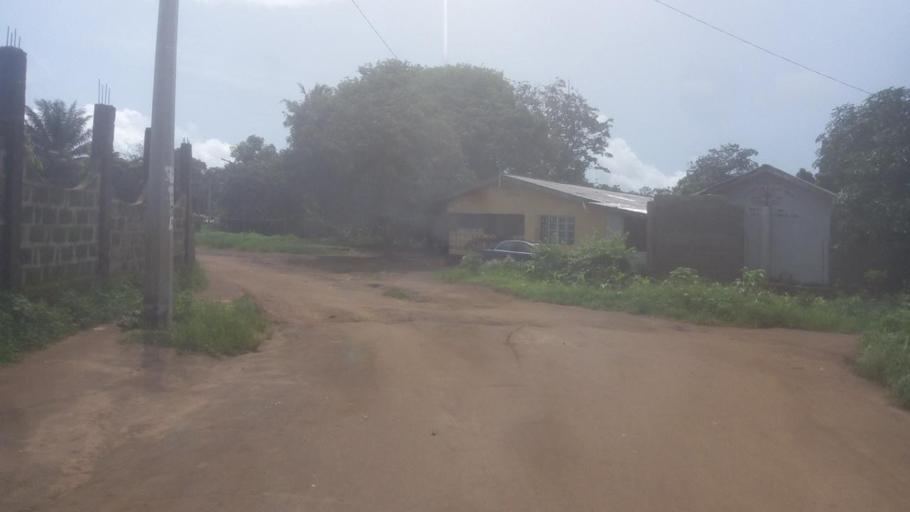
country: SL
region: Northern Province
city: Tintafor
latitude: 8.6332
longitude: -13.2175
